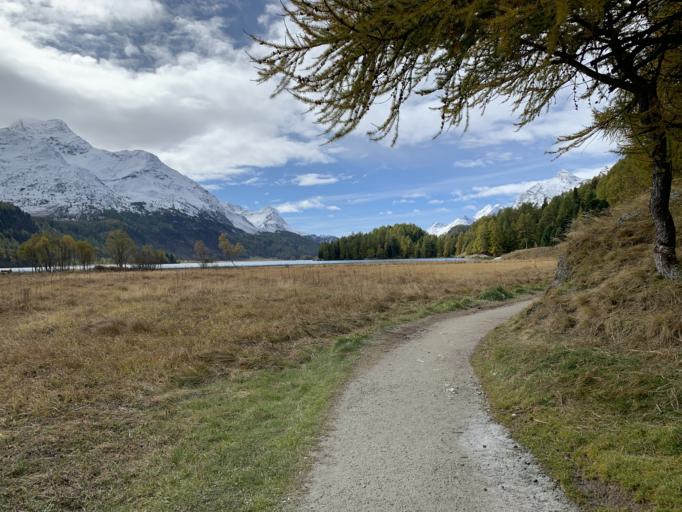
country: CH
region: Grisons
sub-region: Maloja District
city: Silvaplana
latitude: 46.4292
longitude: 9.7524
